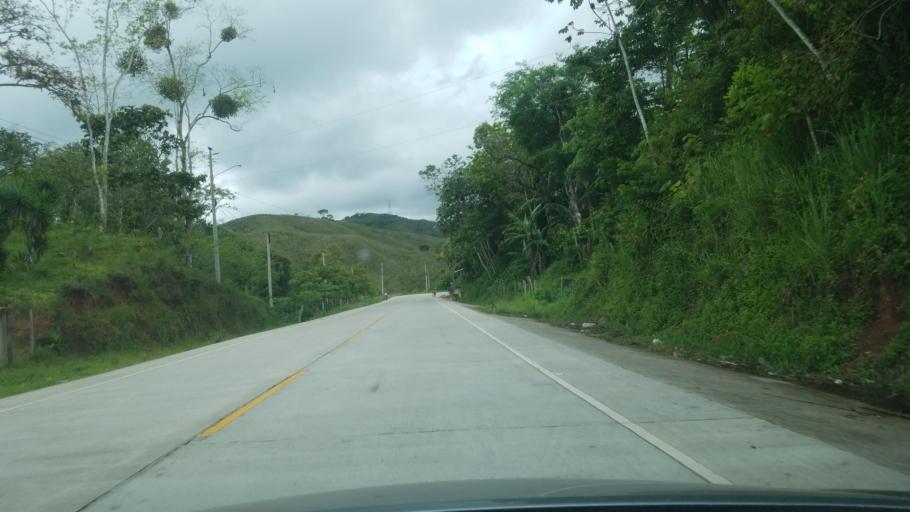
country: HN
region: Copan
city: San Jeronimo
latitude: 14.9423
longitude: -88.9151
